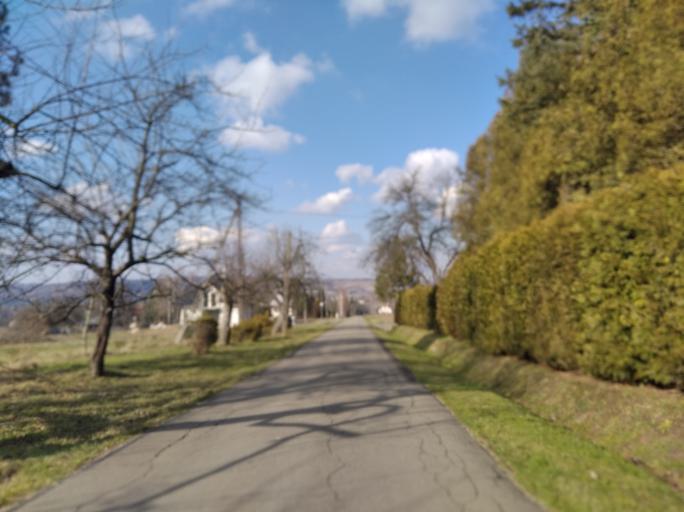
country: PL
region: Subcarpathian Voivodeship
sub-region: Powiat strzyzowski
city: Wysoka Strzyzowska
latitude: 49.8525
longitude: 21.7097
